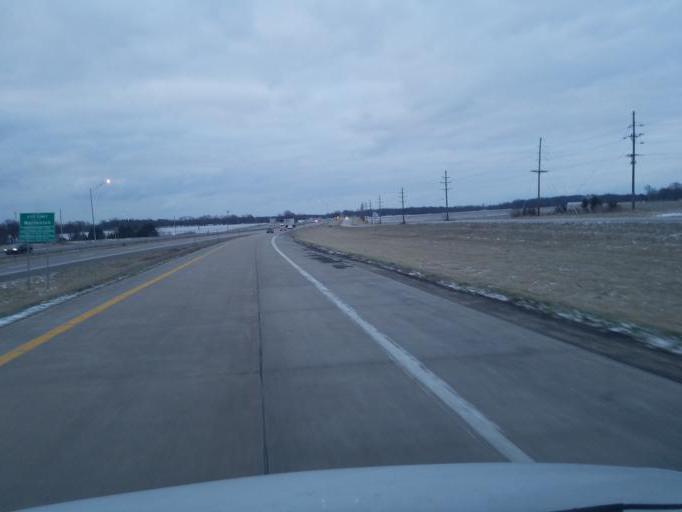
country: US
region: Missouri
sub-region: Warren County
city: Warrenton
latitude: 38.8377
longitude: -91.2238
